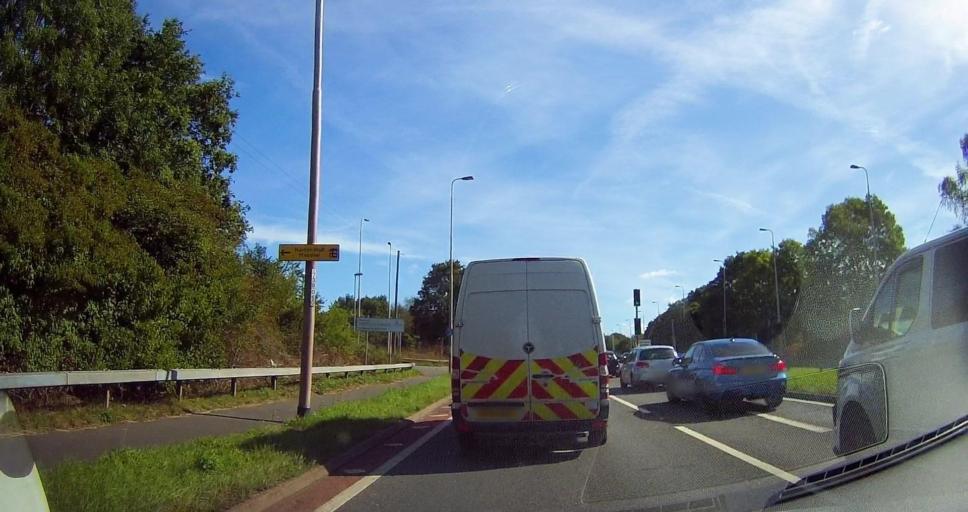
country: GB
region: England
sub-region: Staffordshire
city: Great Wyrley
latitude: 52.6661
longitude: -1.9961
